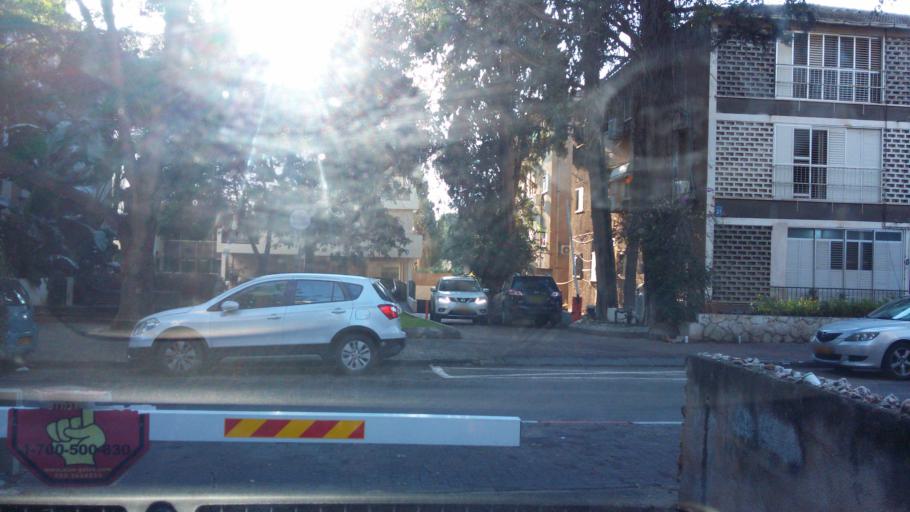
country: IL
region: Tel Aviv
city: Herzliyya
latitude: 32.1694
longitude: 34.8397
